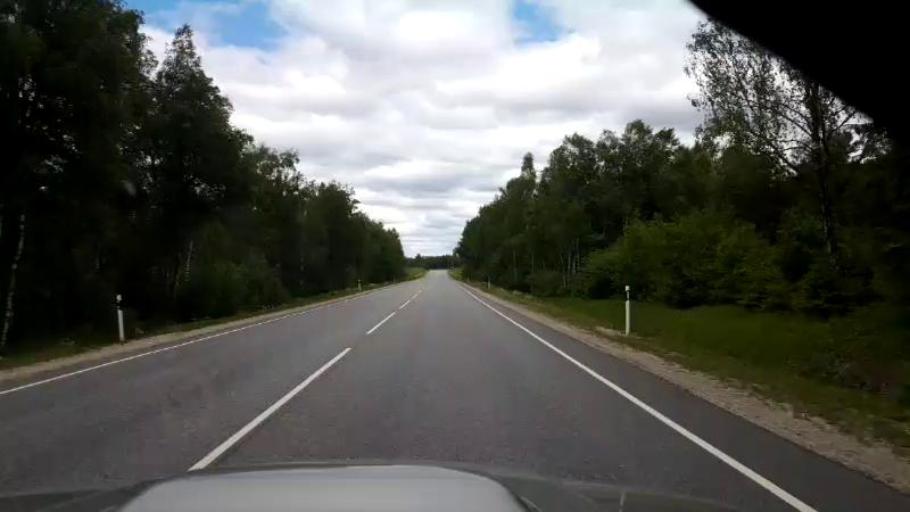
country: EE
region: Raplamaa
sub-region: Maerjamaa vald
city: Marjamaa
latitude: 58.9582
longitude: 24.4736
